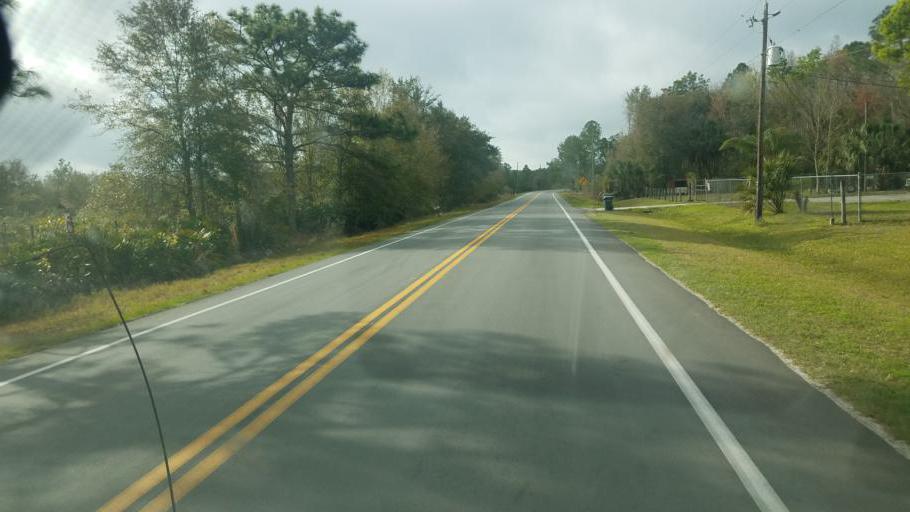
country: US
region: Florida
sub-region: Polk County
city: Gibsonia
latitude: 28.2174
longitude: -81.9822
